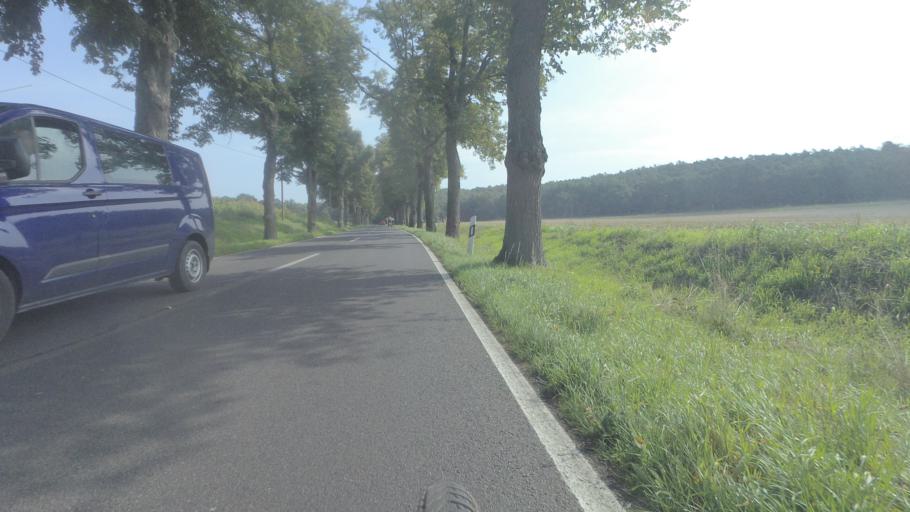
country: DE
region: Brandenburg
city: Mittenwalde
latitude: 52.2702
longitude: 13.4995
